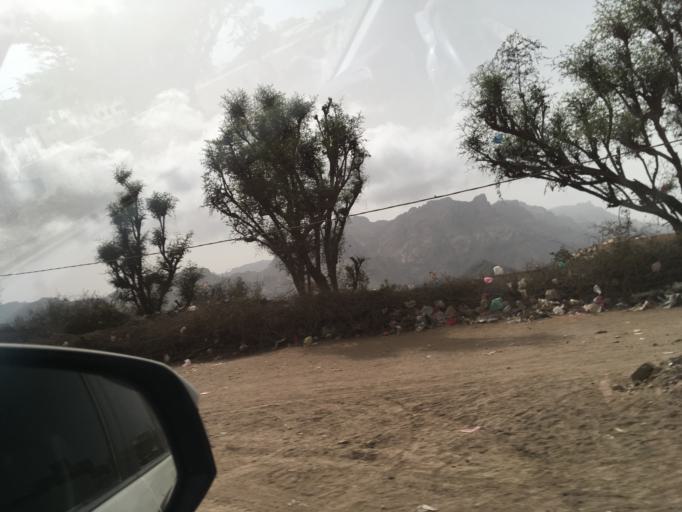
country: YE
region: Ad Dali'
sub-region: Ad Dhale'e
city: Dhalie
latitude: 13.7061
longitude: 44.7360
